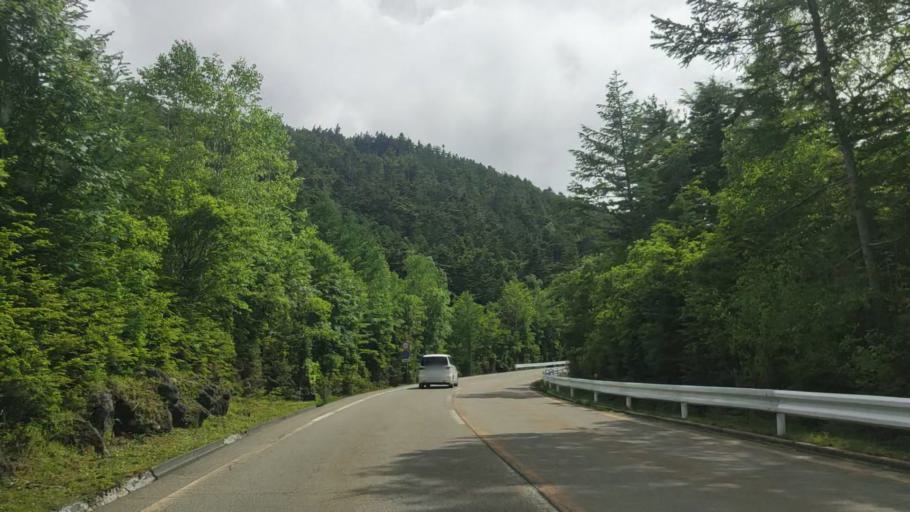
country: JP
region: Yamanashi
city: Fujikawaguchiko
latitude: 35.4041
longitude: 138.6982
